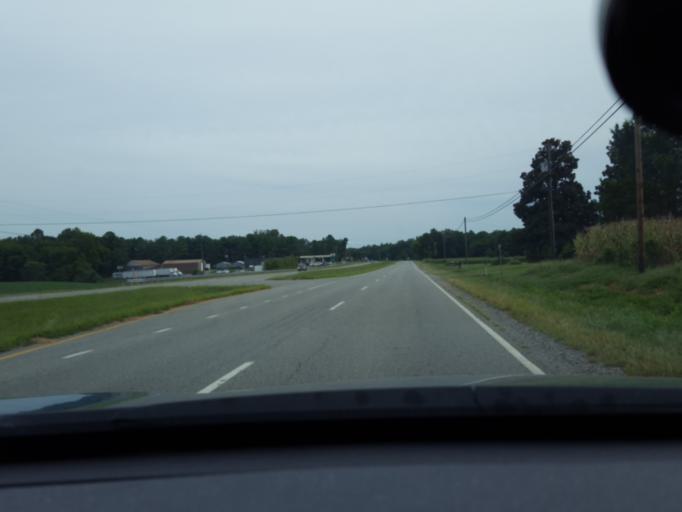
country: US
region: Virginia
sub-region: Caroline County
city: Bowling Green
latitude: 38.0152
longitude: -77.3369
